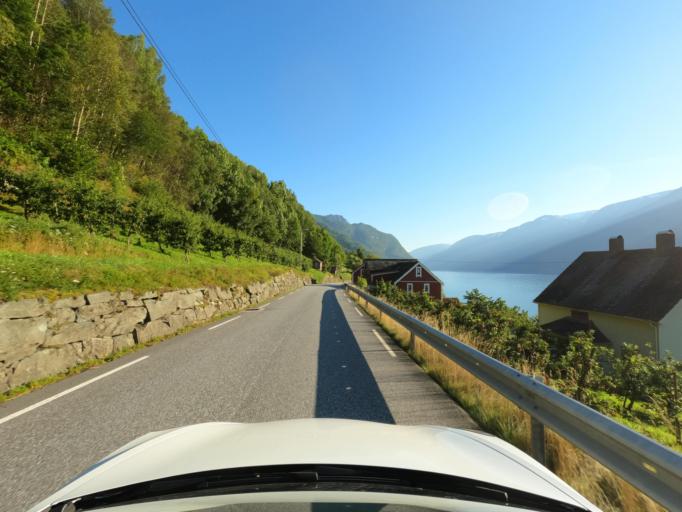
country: NO
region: Hordaland
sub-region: Odda
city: Odda
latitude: 60.2202
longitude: 6.6036
